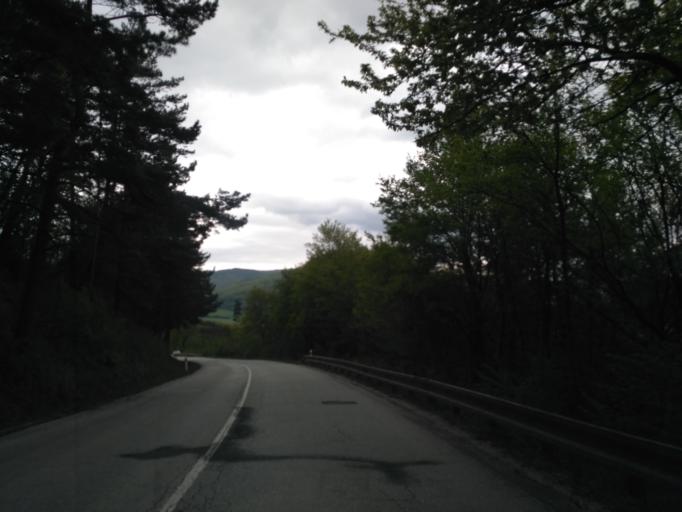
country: SK
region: Kosicky
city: Dobsina
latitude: 48.6443
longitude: 20.3601
